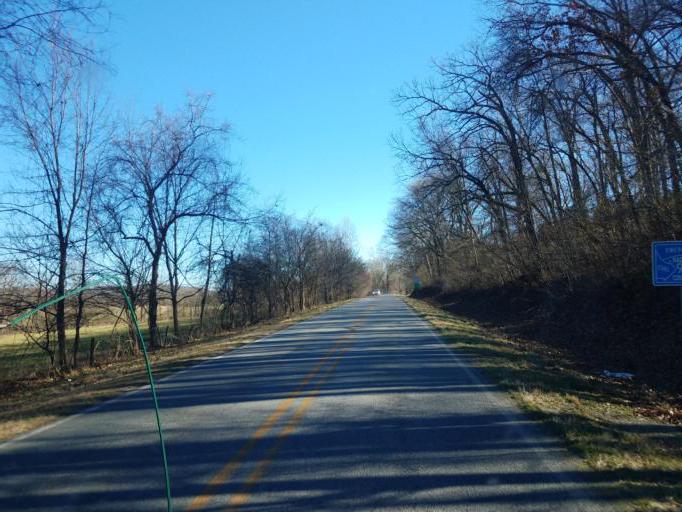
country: US
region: Arkansas
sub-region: Washington County
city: Elkins
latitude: 36.0332
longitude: -93.9453
